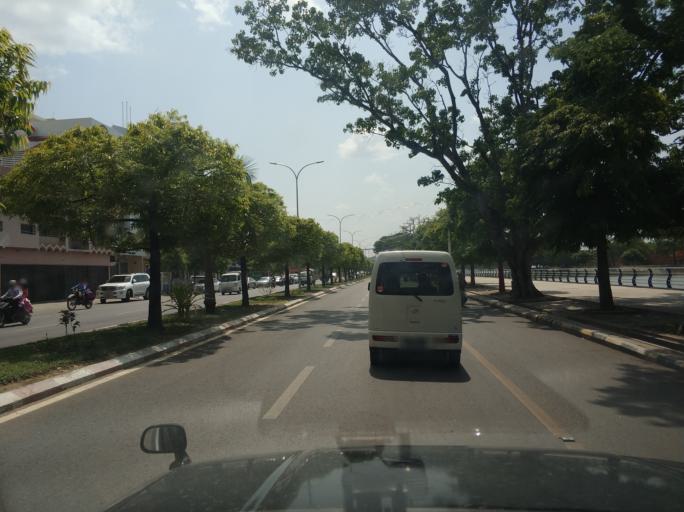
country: MM
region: Mandalay
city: Mandalay
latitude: 21.9826
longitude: 96.0949
